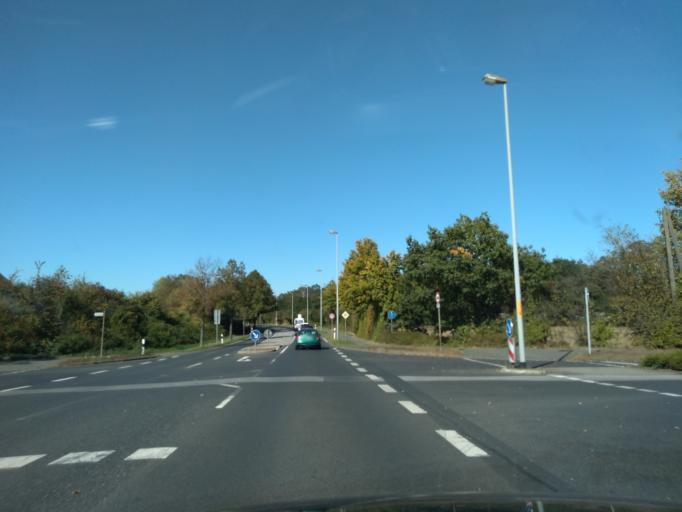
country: DE
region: North Rhine-Westphalia
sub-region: Regierungsbezirk Dusseldorf
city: Dinslaken
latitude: 51.5490
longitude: 6.7558
